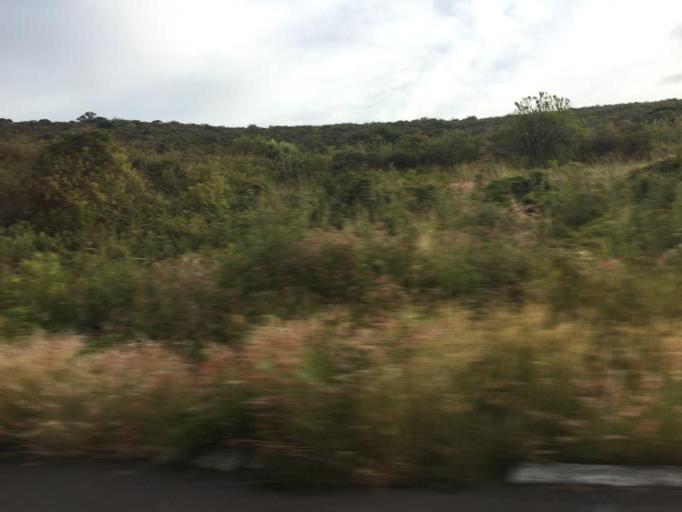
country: MX
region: Michoacan
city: Copandaro de Galeana
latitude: 19.9029
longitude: -101.2698
